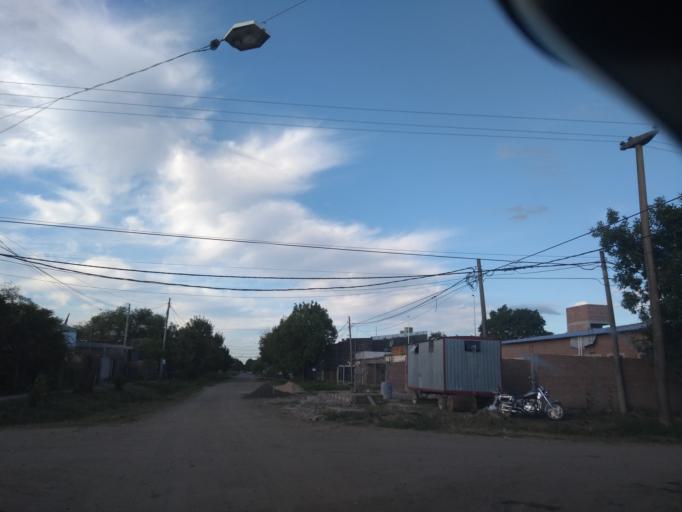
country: AR
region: Chaco
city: Barranqueras
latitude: -27.4900
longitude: -58.9370
